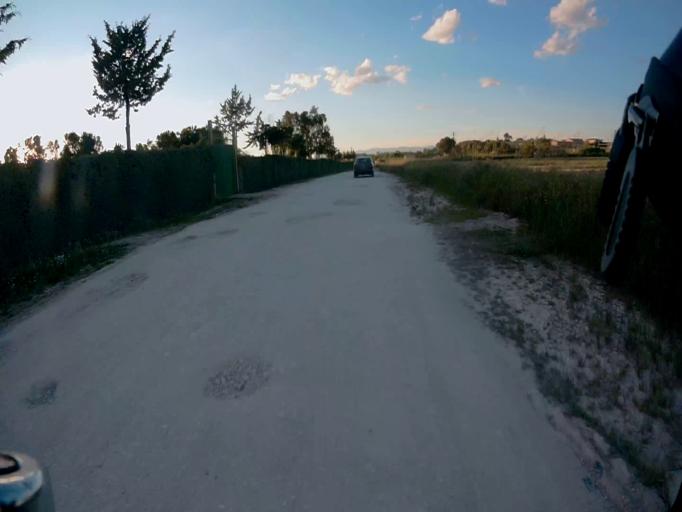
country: ES
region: Madrid
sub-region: Provincia de Madrid
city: Alcorcon
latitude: 40.3328
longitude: -3.7959
